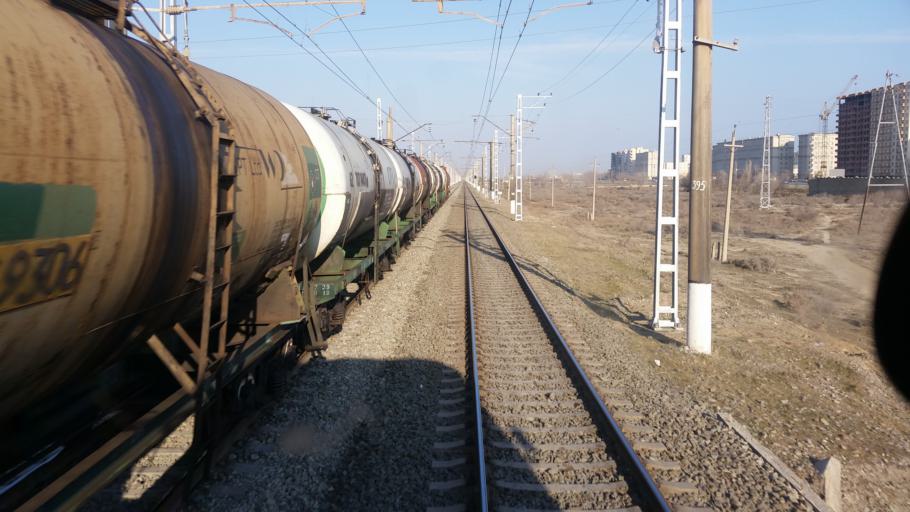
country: AZ
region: Baki
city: Korgoz
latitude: 40.2279
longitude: 49.5694
